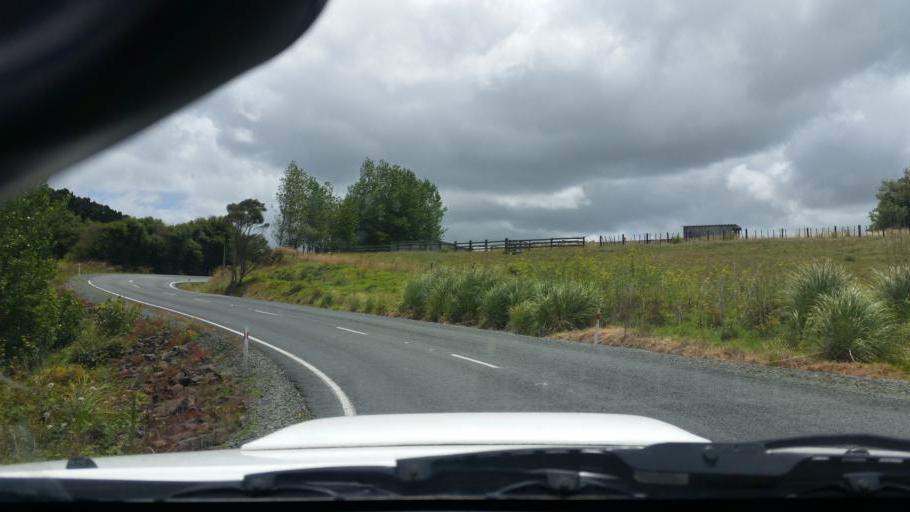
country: NZ
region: Auckland
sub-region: Auckland
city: Wellsford
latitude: -36.1268
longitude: 174.3284
